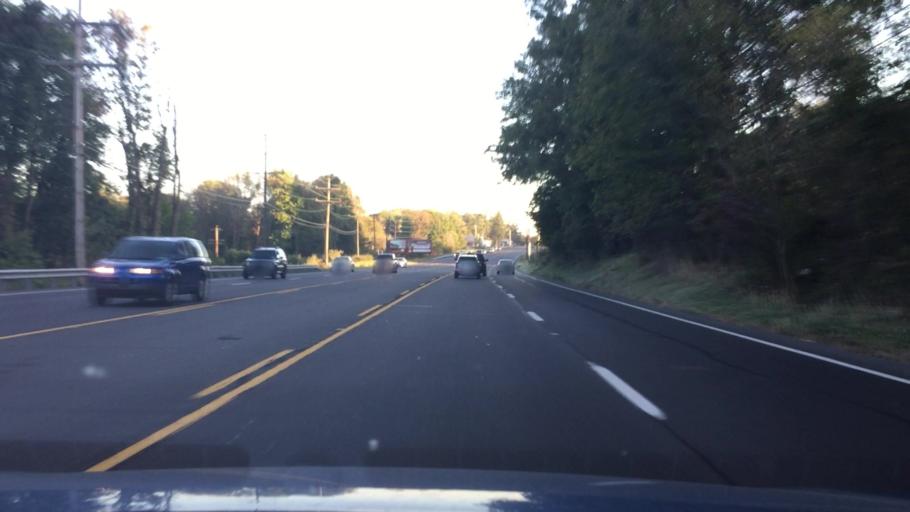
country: US
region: Pennsylvania
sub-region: Lehigh County
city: Coopersburg
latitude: 40.4959
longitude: -75.3823
